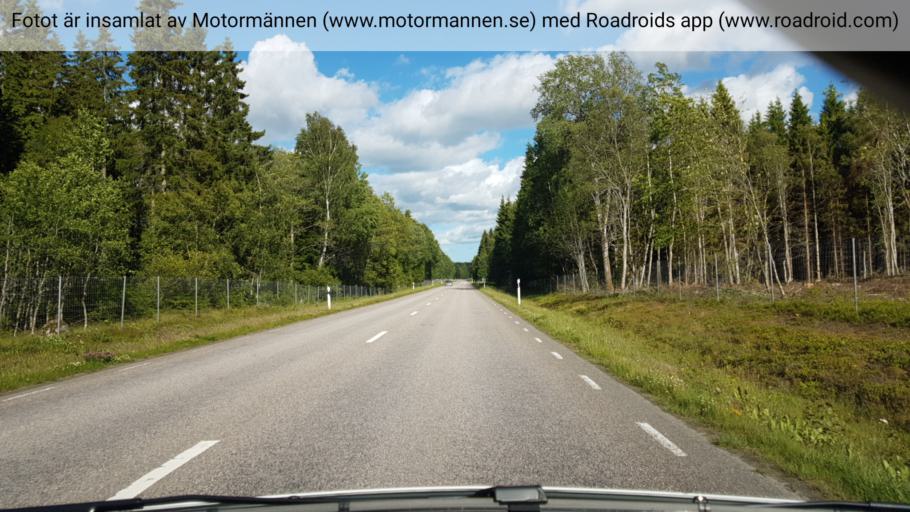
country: SE
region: Vaestra Goetaland
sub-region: Falkopings Kommun
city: Floby
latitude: 58.2081
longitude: 13.2806
